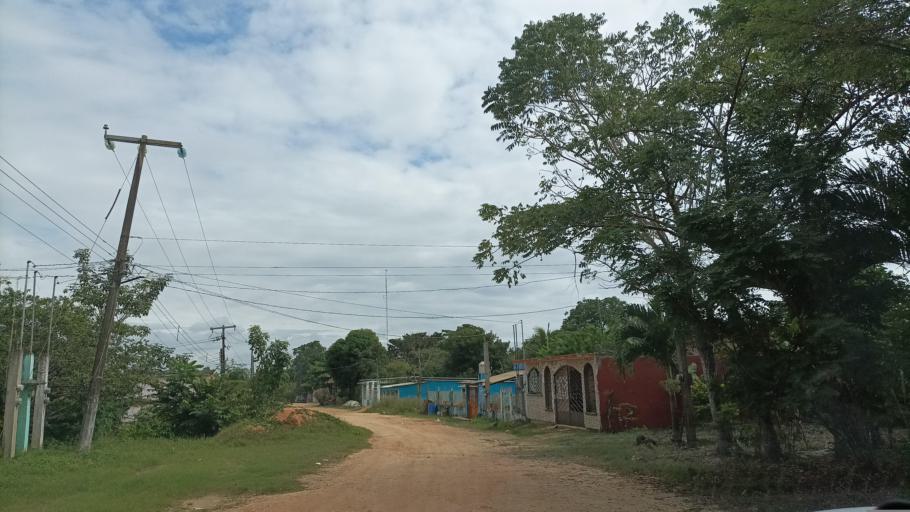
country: MX
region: Veracruz
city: Texistepec
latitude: 17.9590
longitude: -94.8152
